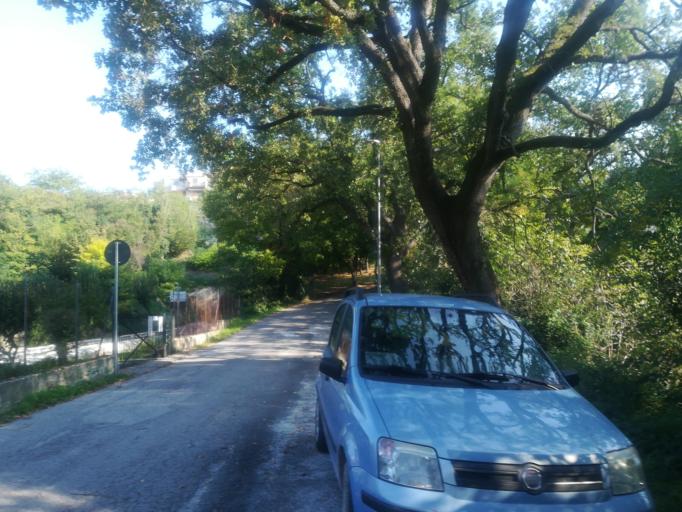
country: IT
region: The Marches
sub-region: Provincia di Macerata
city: Macerata
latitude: 43.2972
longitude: 13.4447
